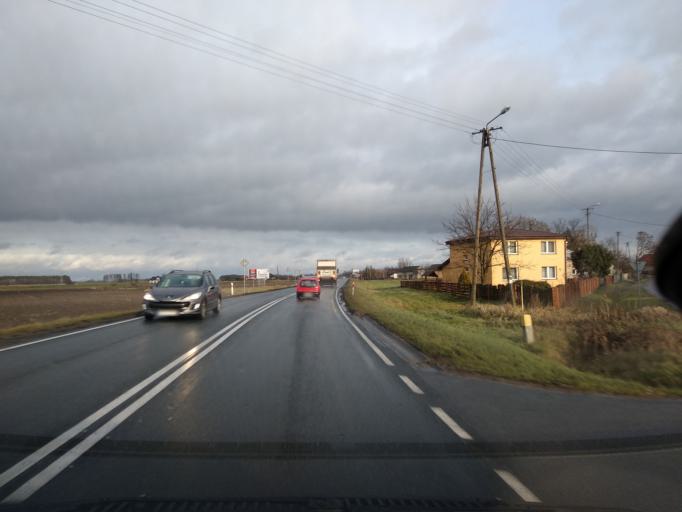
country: PL
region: Greater Poland Voivodeship
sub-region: Powiat koninski
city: Rychwal
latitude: 52.1228
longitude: 18.1709
